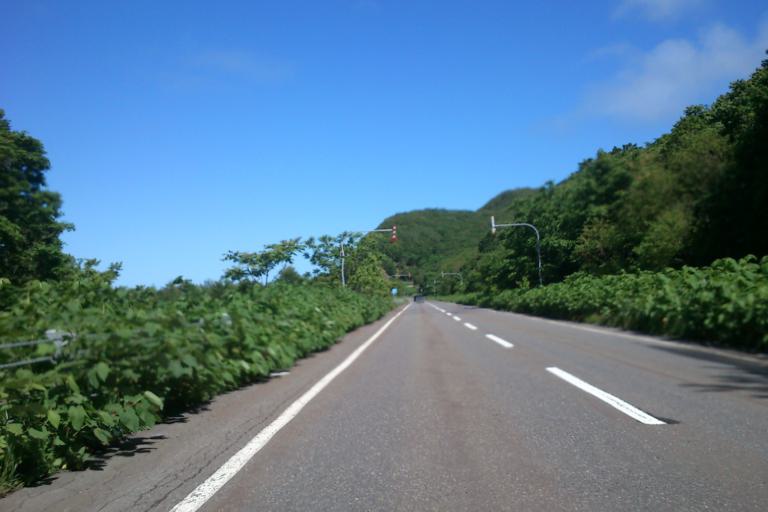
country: JP
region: Hokkaido
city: Ishikari
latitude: 43.4866
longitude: 141.3829
